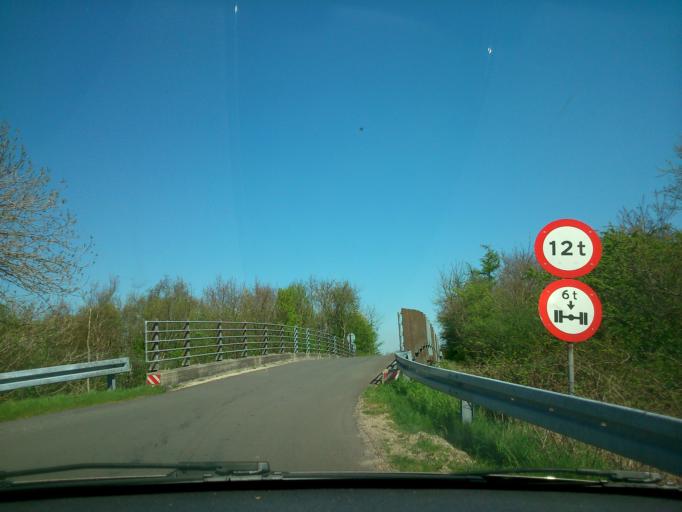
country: DK
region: South Denmark
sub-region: Varde Kommune
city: Olgod
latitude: 55.8430
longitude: 8.5851
